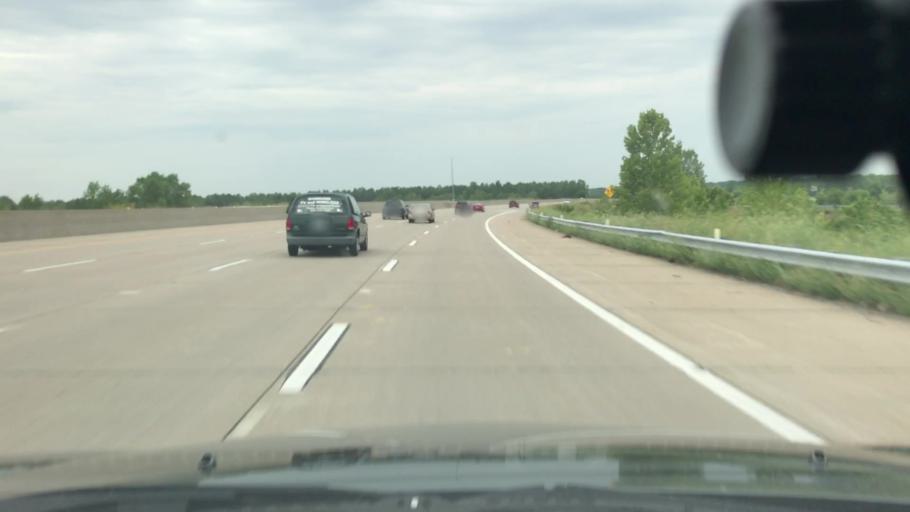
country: US
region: Missouri
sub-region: Saint Louis County
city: Maryland Heights
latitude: 38.7072
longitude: -90.4996
